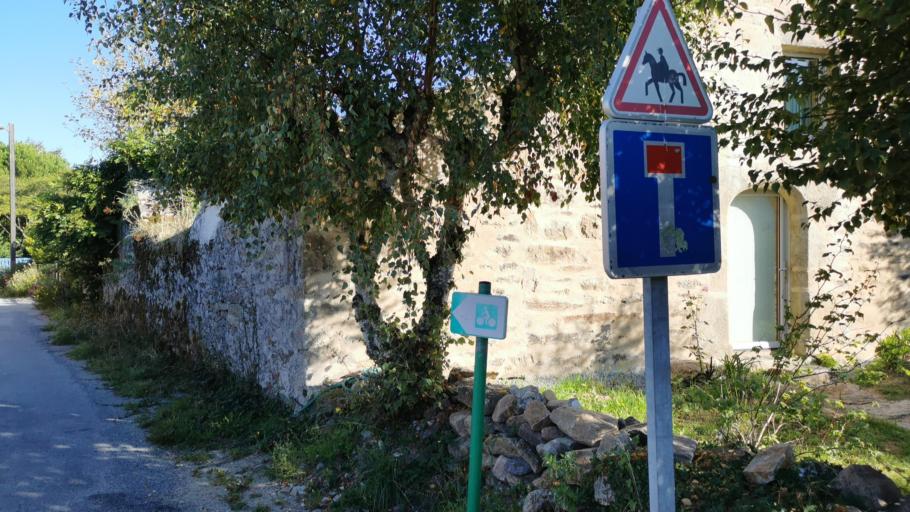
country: FR
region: Brittany
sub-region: Departement du Morbihan
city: Saint-Gildas-de-Rhuys
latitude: 47.5347
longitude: -2.8522
